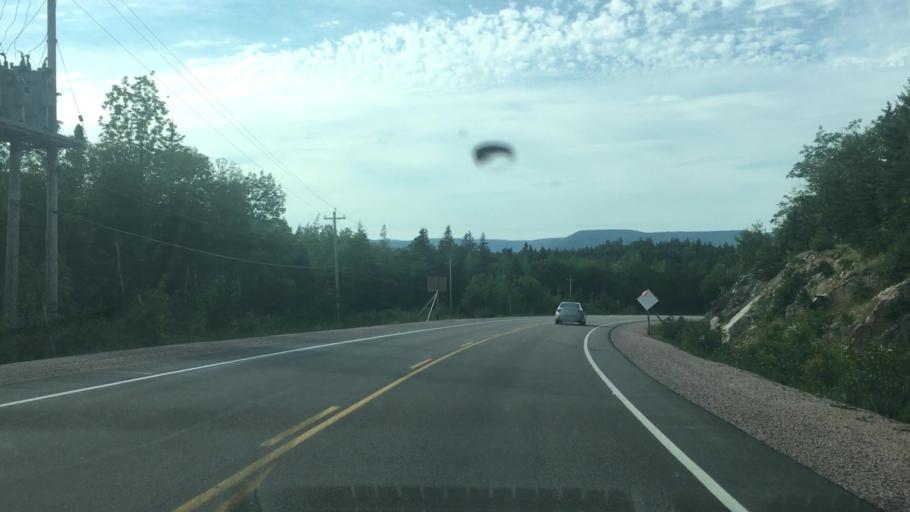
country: CA
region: Nova Scotia
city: Sydney Mines
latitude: 46.8574
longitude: -60.4621
